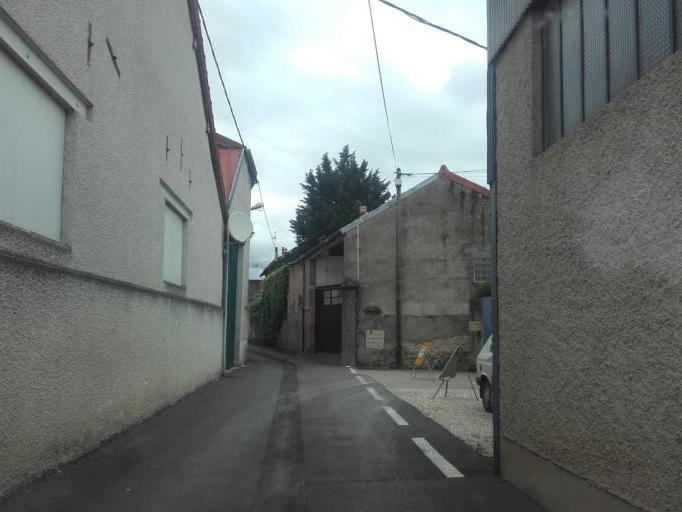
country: FR
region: Bourgogne
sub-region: Departement de la Cote-d'Or
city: Beaune
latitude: 47.0183
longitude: 4.8421
